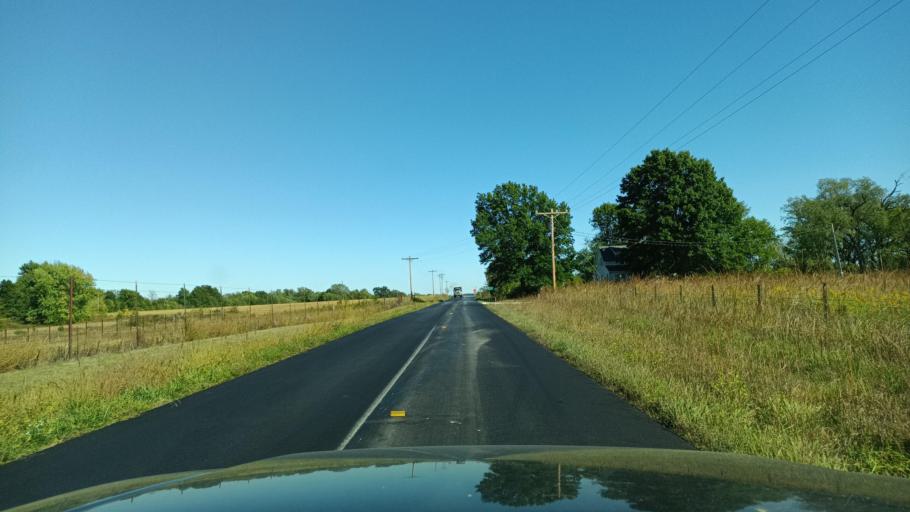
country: US
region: Missouri
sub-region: Macon County
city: La Plata
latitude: 39.9281
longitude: -92.5728
